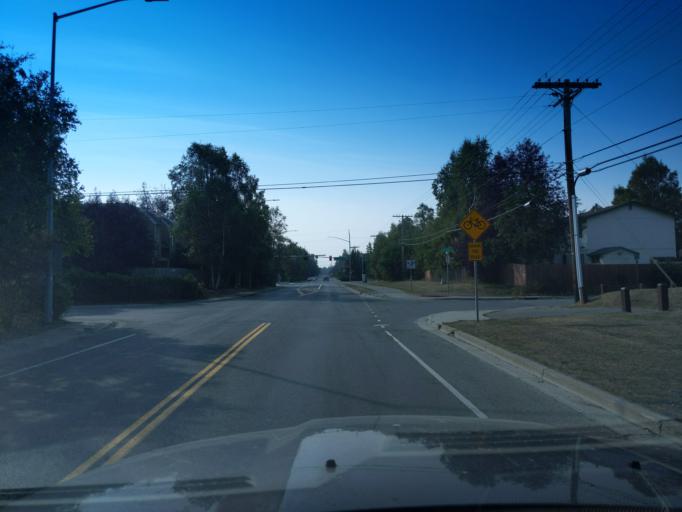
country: US
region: Alaska
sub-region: Anchorage Municipality
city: Anchorage
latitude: 61.1902
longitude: -149.9429
